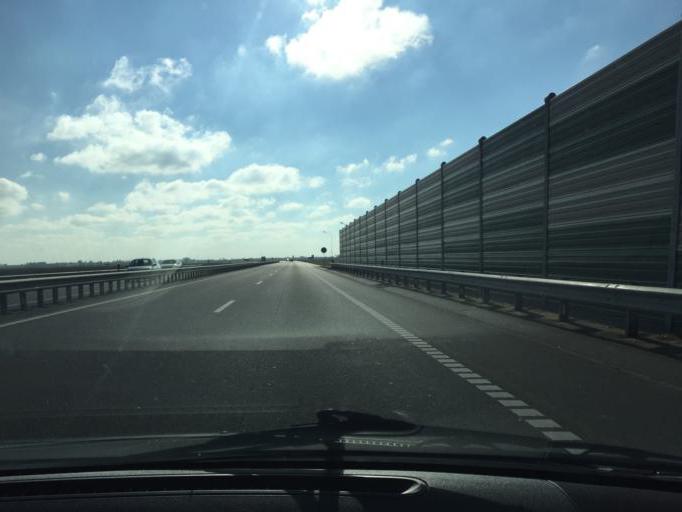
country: BY
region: Minsk
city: Slutsk
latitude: 53.1437
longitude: 27.5520
